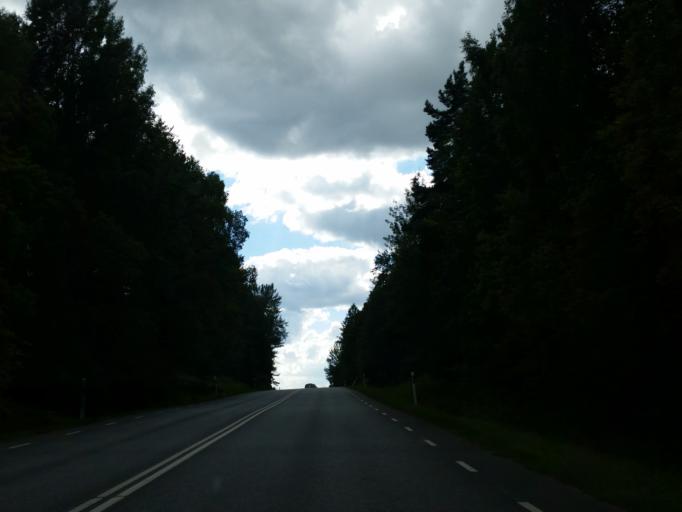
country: SE
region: Soedermanland
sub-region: Trosa Kommun
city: Vagnharad
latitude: 58.9558
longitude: 17.5554
